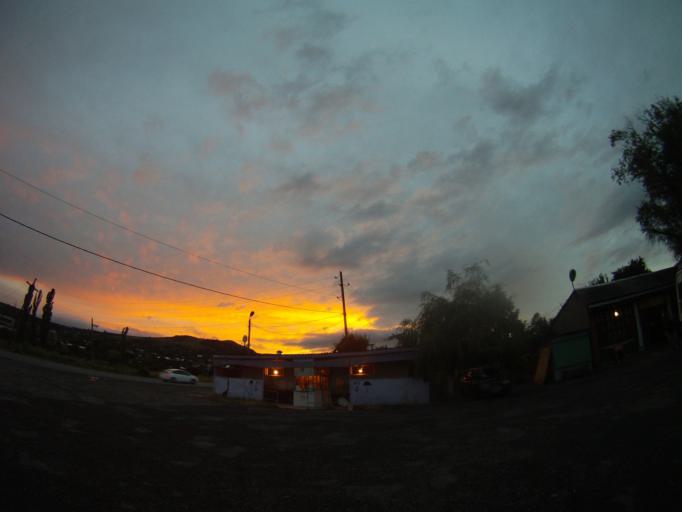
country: GE
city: Surami
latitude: 42.0142
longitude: 43.5742
